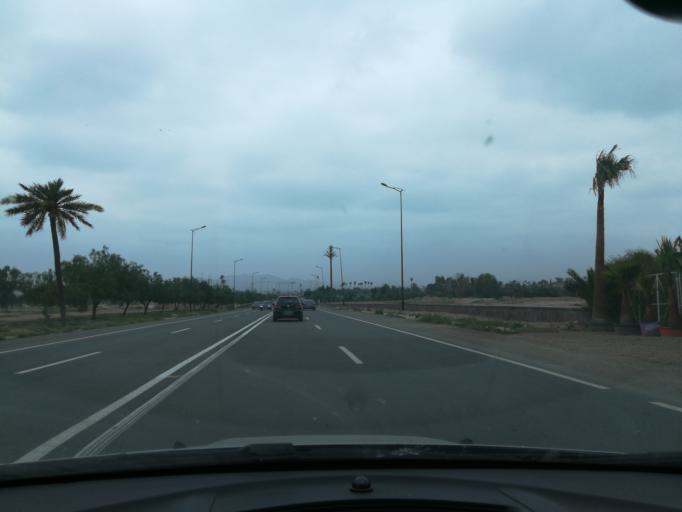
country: MA
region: Marrakech-Tensift-Al Haouz
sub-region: Marrakech
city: Marrakesh
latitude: 31.6655
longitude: -7.9899
